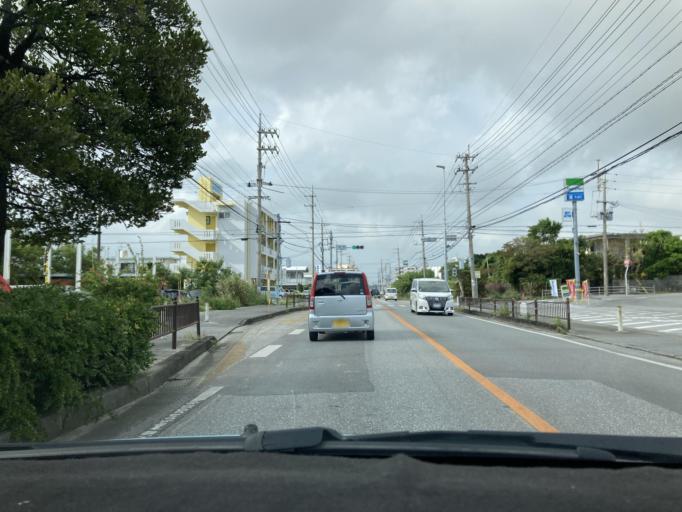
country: JP
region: Okinawa
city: Itoman
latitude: 26.1568
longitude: 127.6707
